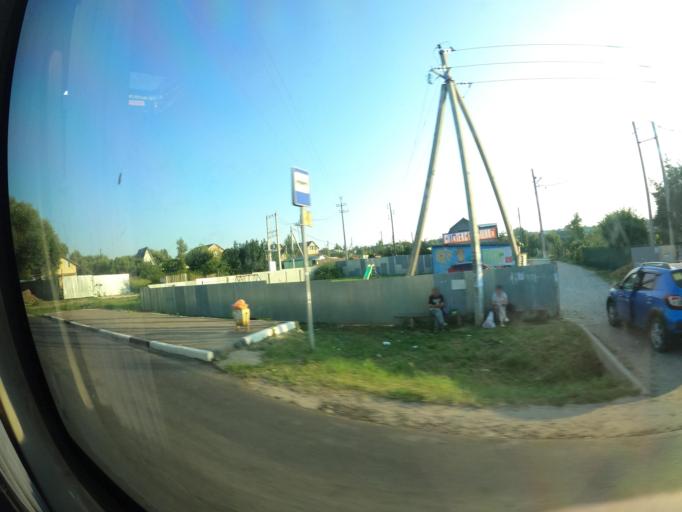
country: RU
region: Moskovskaya
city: Serpukhov
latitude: 54.9400
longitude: 37.3546
